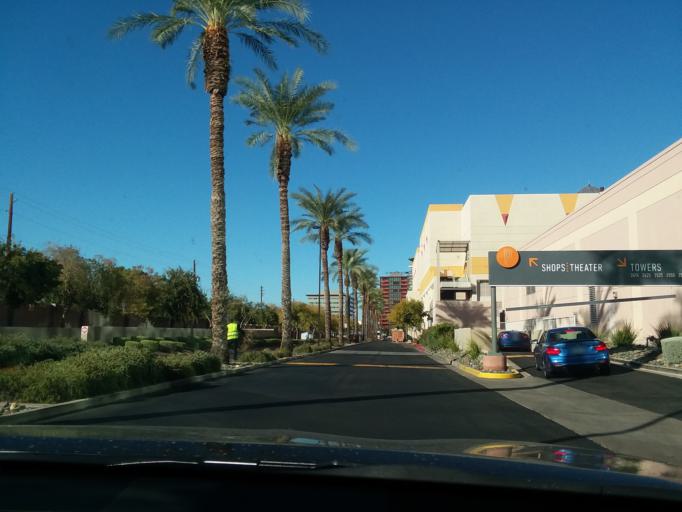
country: US
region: Arizona
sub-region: Maricopa County
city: Phoenix
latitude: 33.5079
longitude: -112.0261
